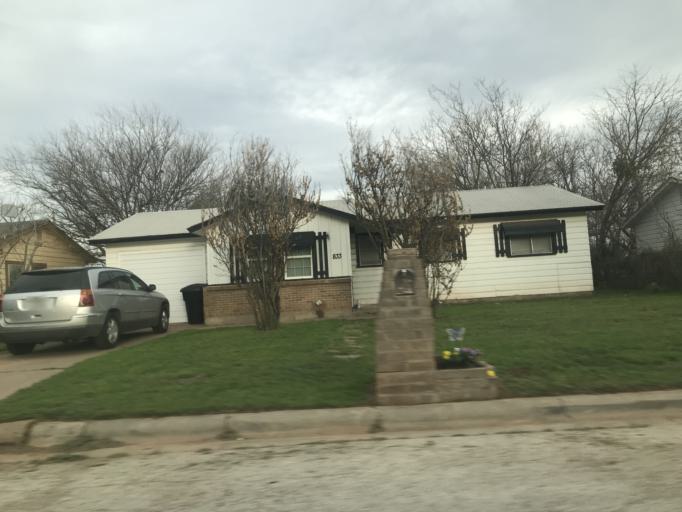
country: US
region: Texas
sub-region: Taylor County
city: Abilene
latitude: 32.4410
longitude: -99.7617
